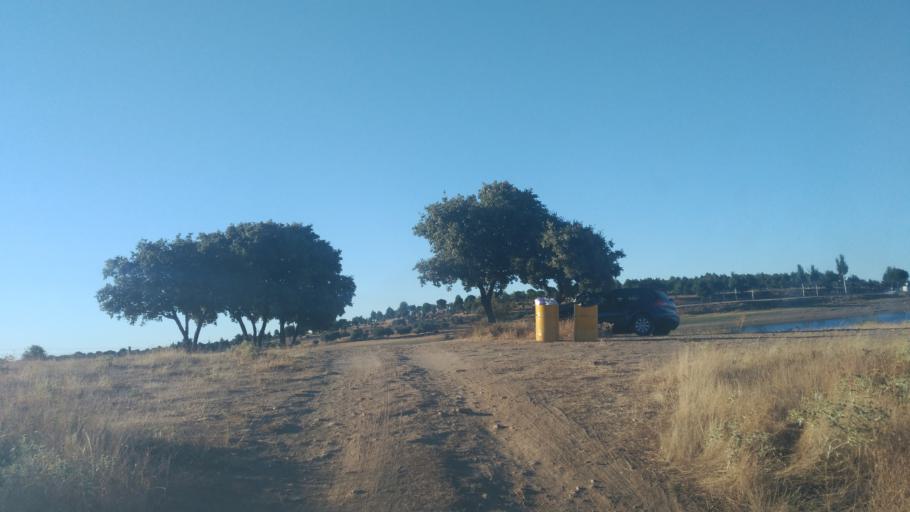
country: ES
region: Castille and Leon
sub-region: Provincia de Salamanca
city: Pelayos
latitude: 40.6634
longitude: -5.6070
